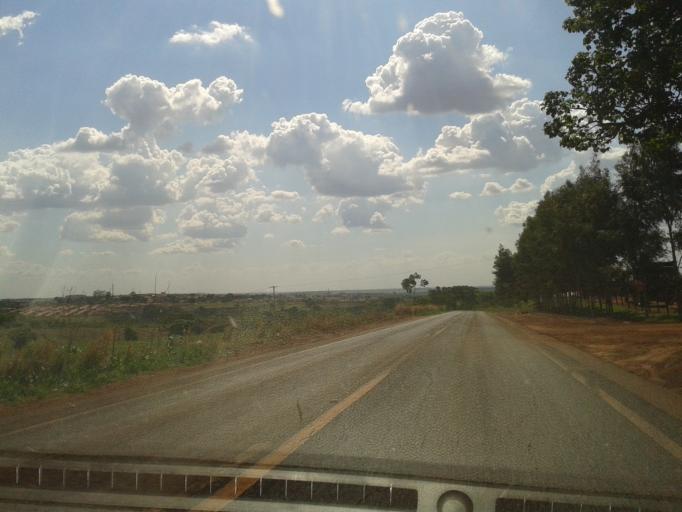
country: BR
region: Minas Gerais
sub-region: Capinopolis
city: Capinopolis
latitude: -18.6813
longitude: -49.5487
